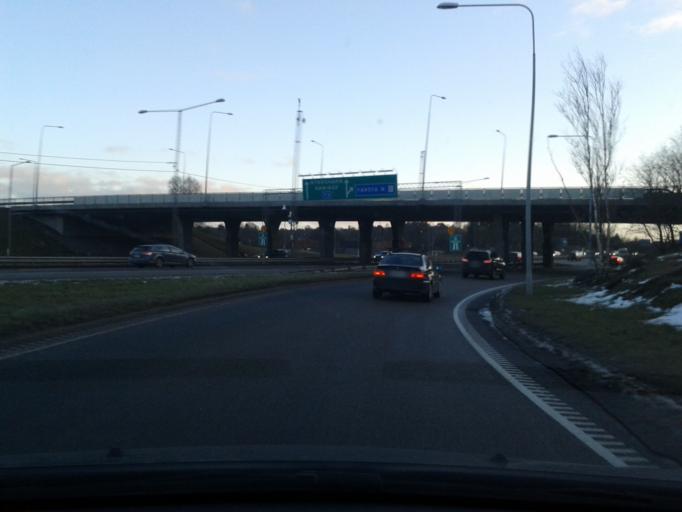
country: SE
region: Stockholm
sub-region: Stockholms Kommun
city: Arsta
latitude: 59.2612
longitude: 18.0985
